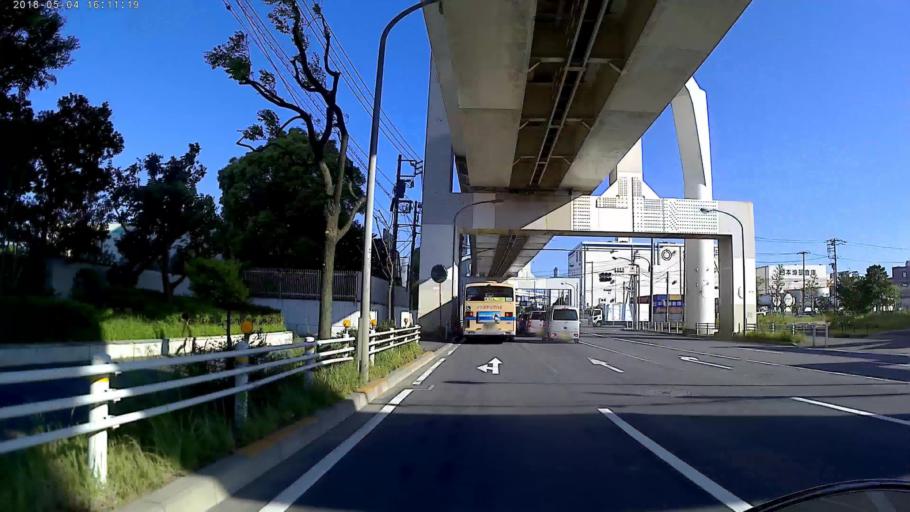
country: JP
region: Kanagawa
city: Yokohama
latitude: 35.4877
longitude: 139.6734
